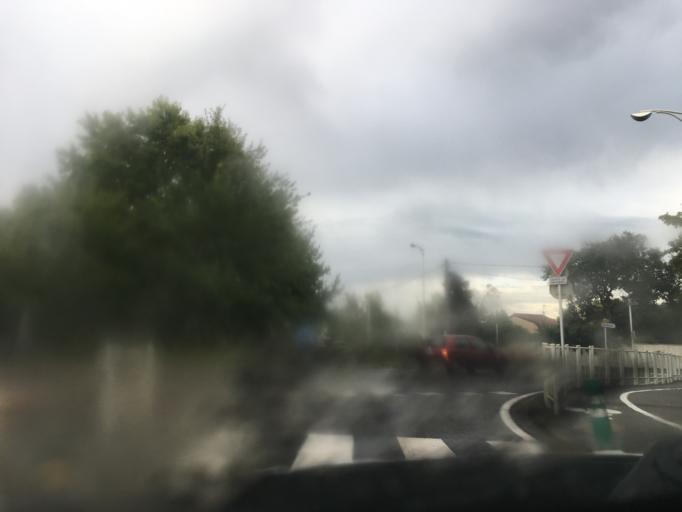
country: FR
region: Midi-Pyrenees
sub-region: Departement de la Haute-Garonne
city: Cugnaux
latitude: 43.5634
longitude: 1.3391
